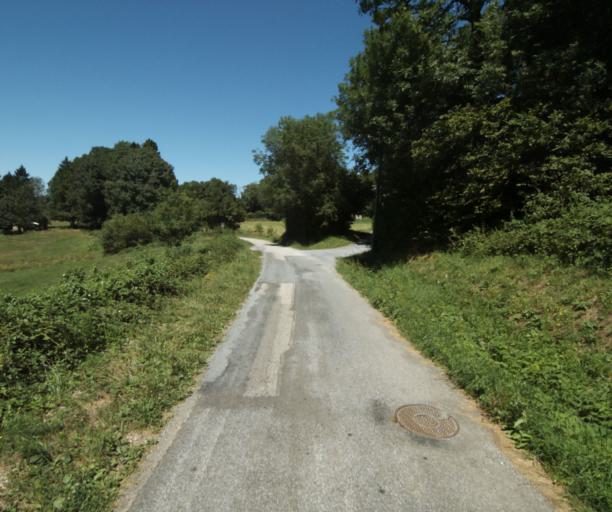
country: FR
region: Midi-Pyrenees
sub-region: Departement du Tarn
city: Dourgne
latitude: 43.4413
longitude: 2.1987
